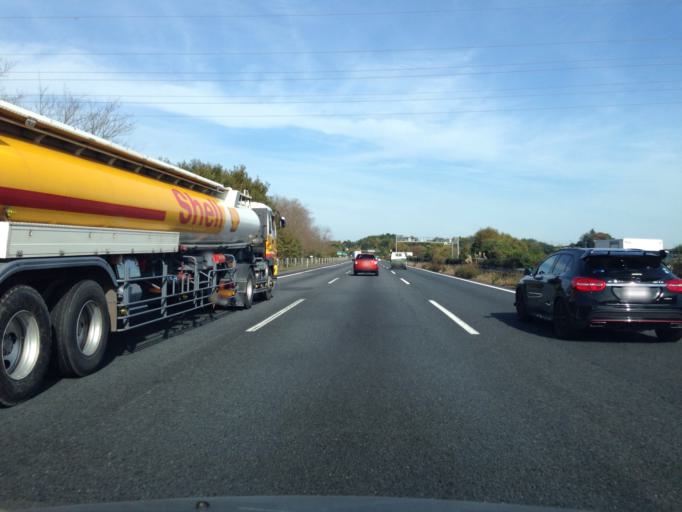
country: JP
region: Ibaraki
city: Ishioka
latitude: 36.1877
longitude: 140.2550
